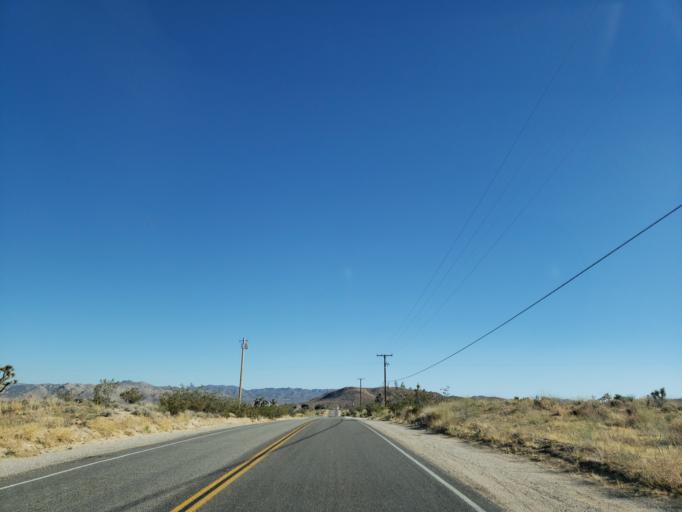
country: US
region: California
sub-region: San Bernardino County
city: Yucca Valley
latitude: 34.1775
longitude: -116.3871
